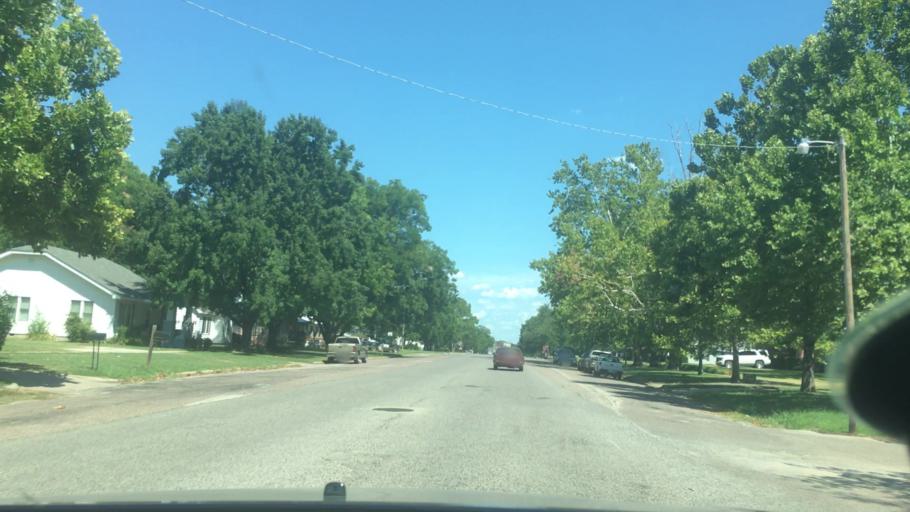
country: US
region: Oklahoma
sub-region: Marshall County
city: Madill
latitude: 34.0921
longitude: -96.7805
